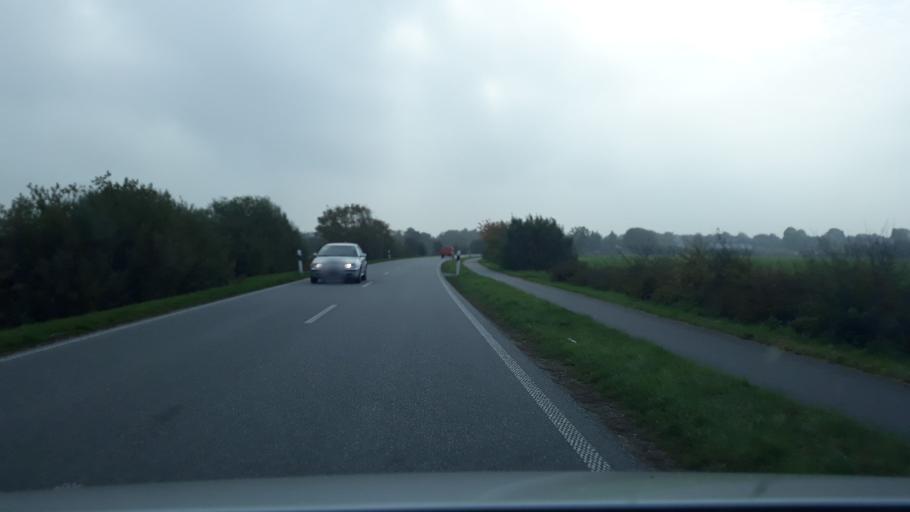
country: DE
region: Schleswig-Holstein
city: Klein Rheide
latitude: 54.4560
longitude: 9.4791
